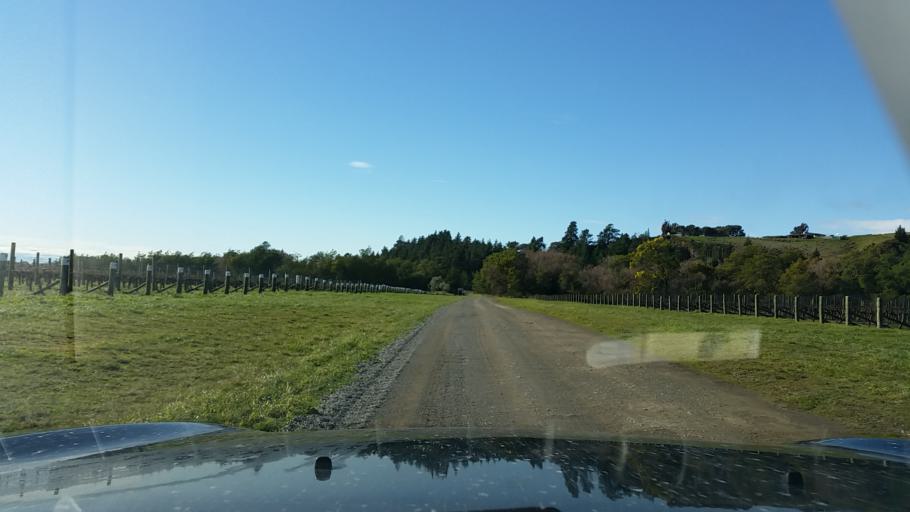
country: NZ
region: Marlborough
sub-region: Marlborough District
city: Blenheim
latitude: -41.5298
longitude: 173.7983
